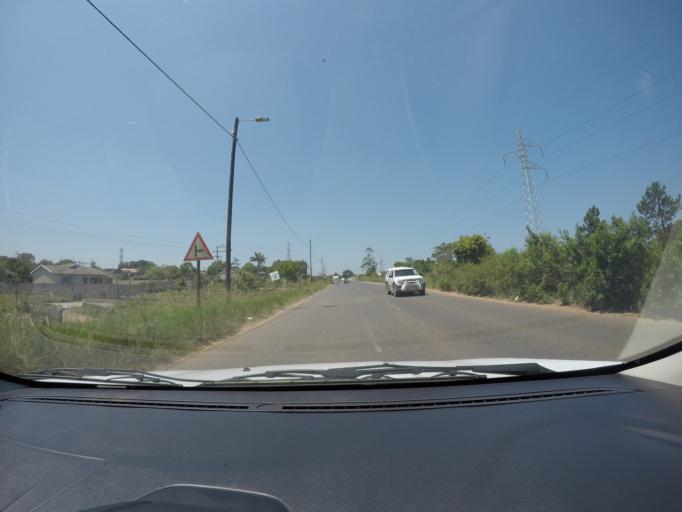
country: ZA
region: KwaZulu-Natal
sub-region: uThungulu District Municipality
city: eSikhawini
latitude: -28.8472
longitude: 31.9304
